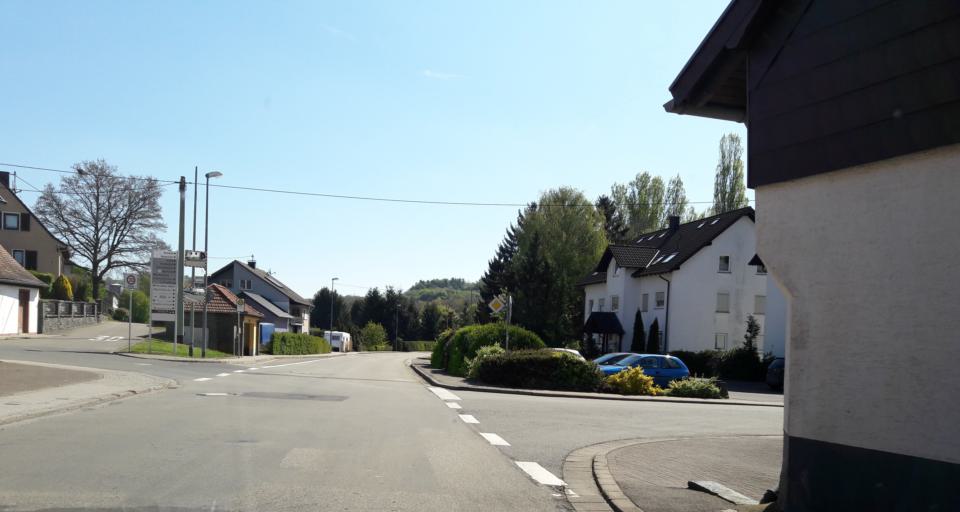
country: DE
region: Rheinland-Pfalz
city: Pfeffelbach
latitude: 49.5406
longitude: 7.3274
